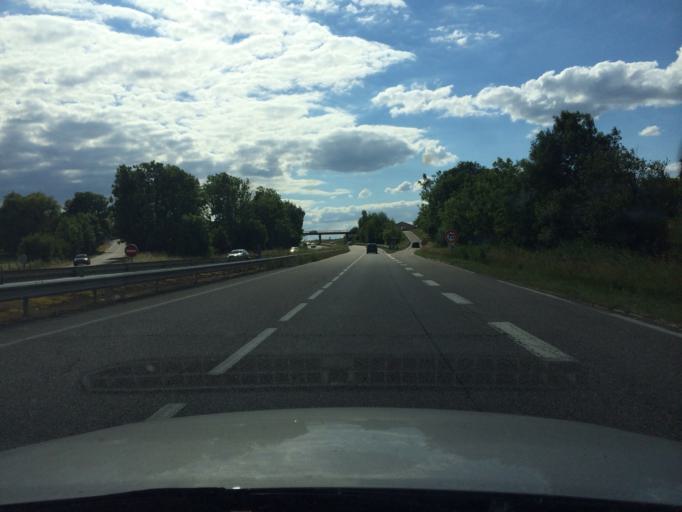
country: FR
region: Lorraine
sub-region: Departement de la Moselle
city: Reding
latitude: 48.7511
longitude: 7.1655
